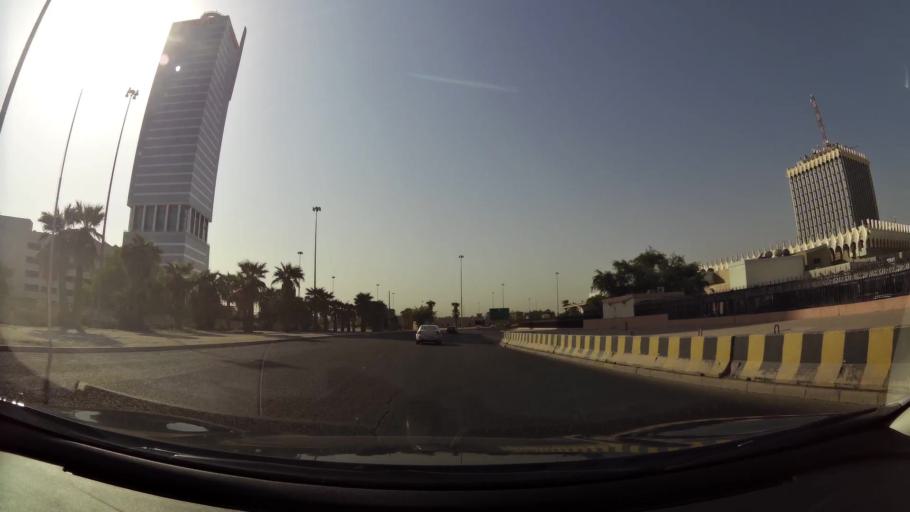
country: KW
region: Al Asimah
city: Kuwait City
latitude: 29.3636
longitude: 47.9743
